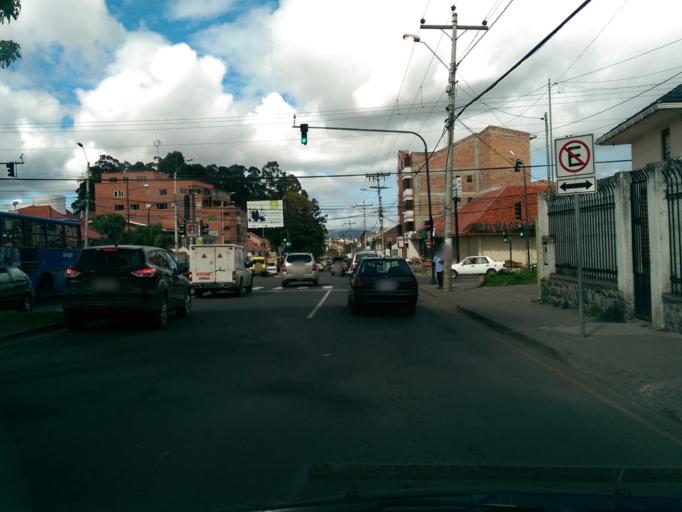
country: EC
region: Azuay
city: Cuenca
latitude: -2.8952
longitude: -79.0196
